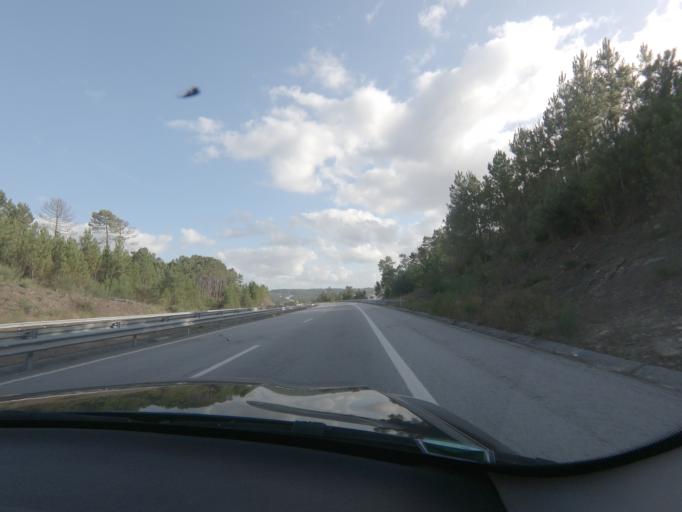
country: PT
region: Viseu
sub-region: Viseu
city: Campo
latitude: 40.7667
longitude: -7.9233
